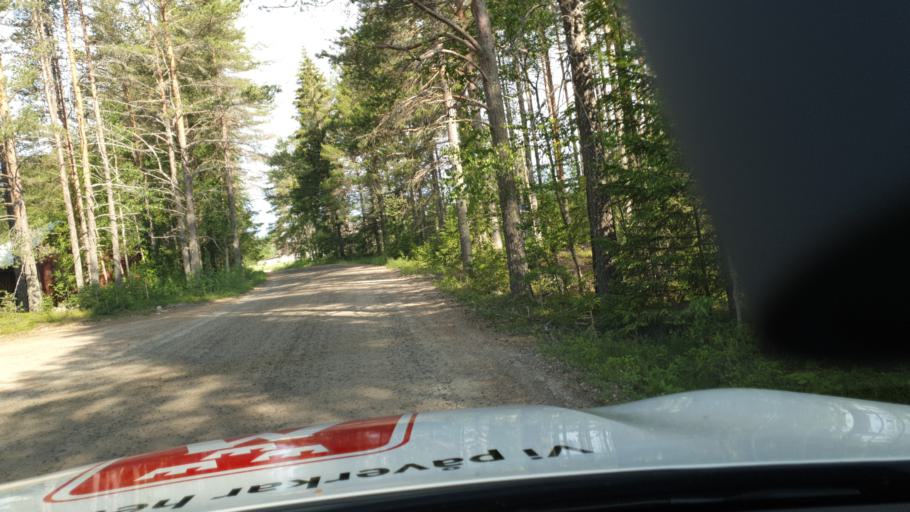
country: SE
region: Vaesterbotten
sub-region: Robertsfors Kommun
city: Robertsfors
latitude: 64.2254
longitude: 21.0232
